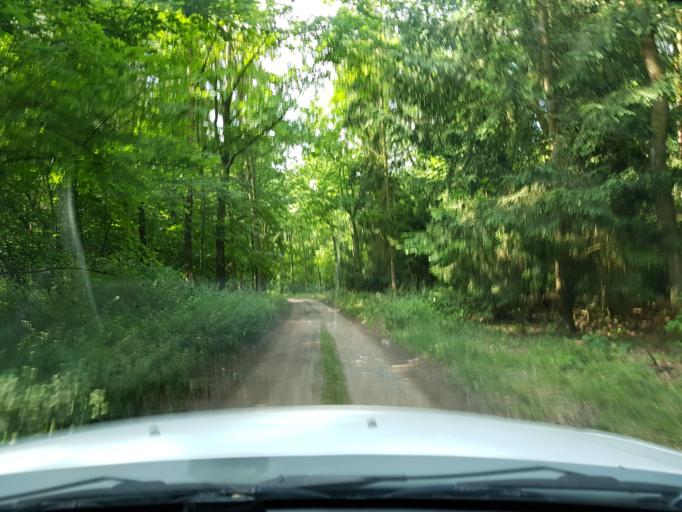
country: PL
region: West Pomeranian Voivodeship
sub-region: Powiat gryfinski
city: Banie
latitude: 53.1568
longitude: 14.6292
